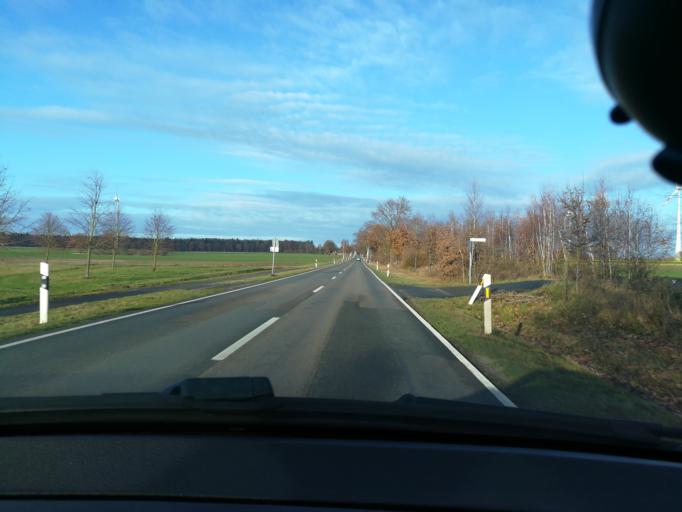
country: DE
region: Lower Saxony
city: Hassel
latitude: 52.7150
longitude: 8.8140
